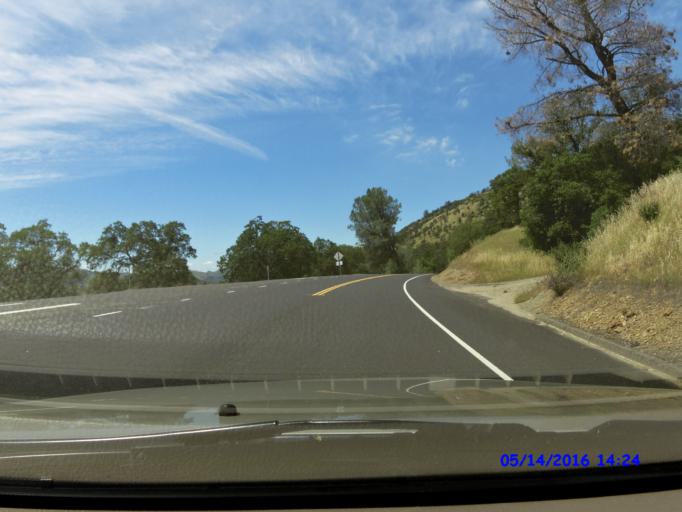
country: US
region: California
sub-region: Tuolumne County
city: Tuolumne City
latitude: 37.6944
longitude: -120.1827
